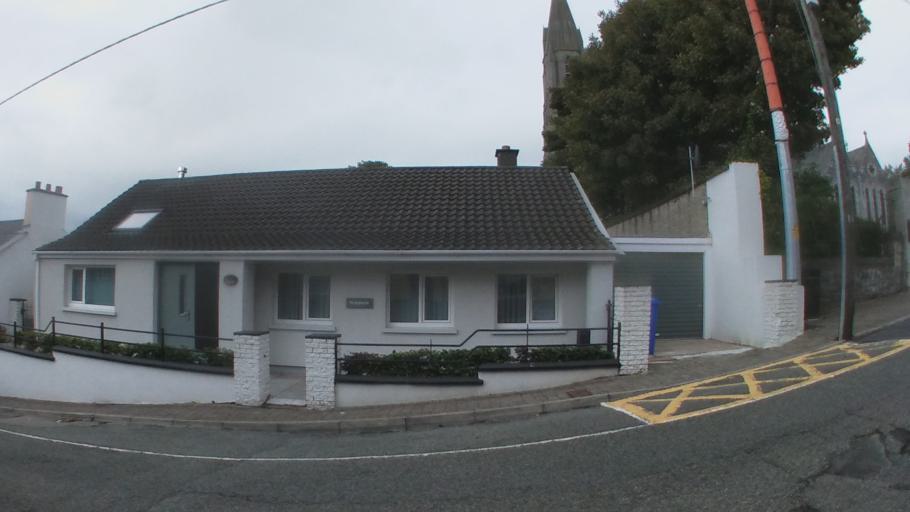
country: IE
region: Leinster
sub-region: Loch Garman
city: New Ross
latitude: 52.3923
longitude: -6.9444
